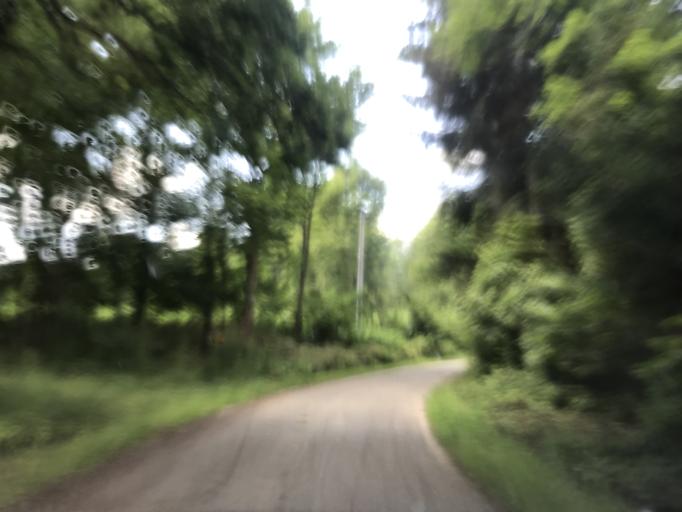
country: PL
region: West Pomeranian Voivodeship
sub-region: Powiat stargardzki
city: Insko
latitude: 53.4937
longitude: 15.4917
